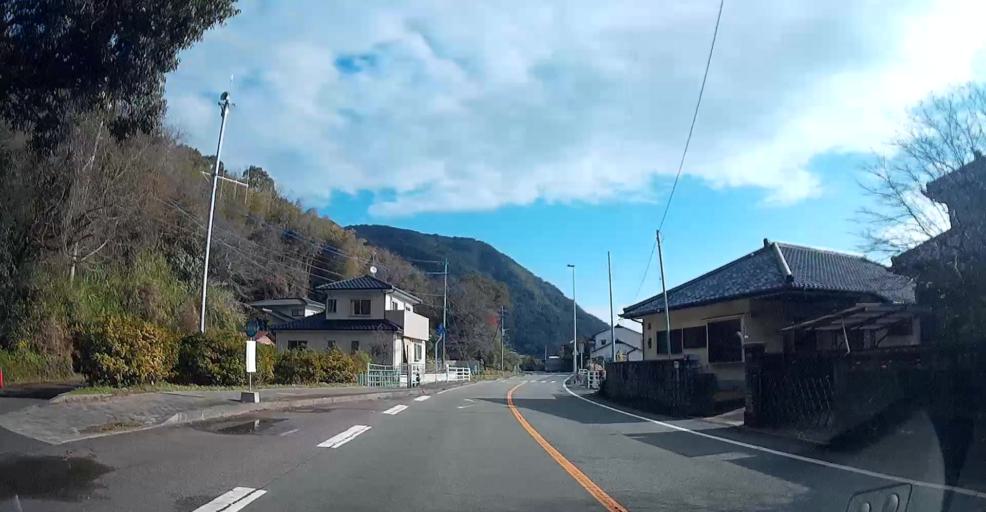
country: JP
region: Kumamoto
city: Yatsushiro
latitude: 32.6199
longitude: 130.4588
